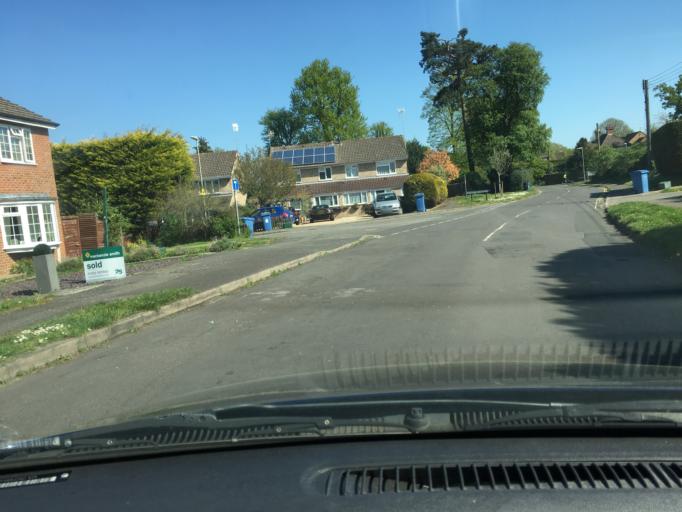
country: GB
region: England
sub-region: Hampshire
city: Yateley
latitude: 51.3369
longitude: -0.8137
